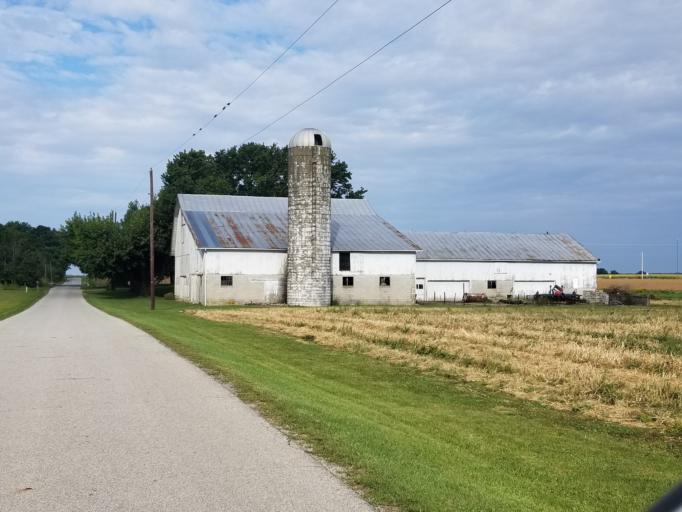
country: US
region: Ohio
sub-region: Crawford County
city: Bucyrus
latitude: 40.7322
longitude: -83.0399
